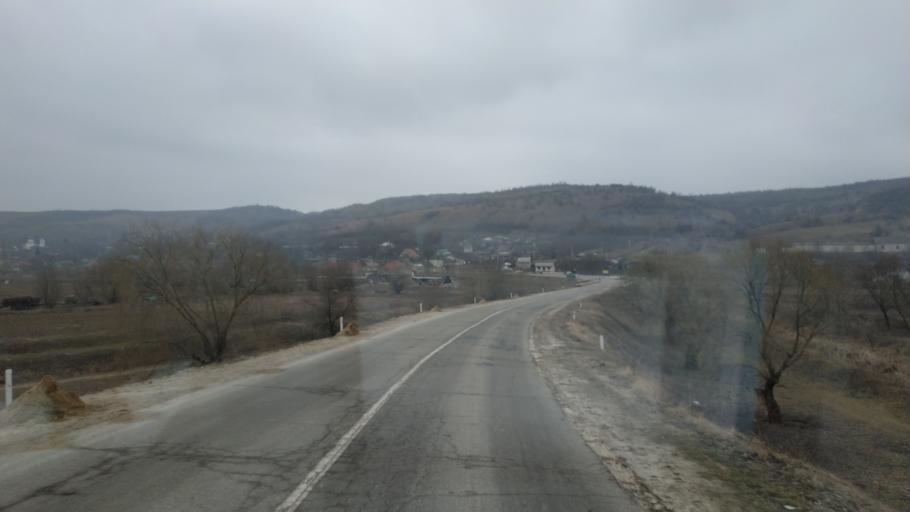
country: MD
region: Stinga Nistrului
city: Bucovat
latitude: 46.9910
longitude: 28.4444
